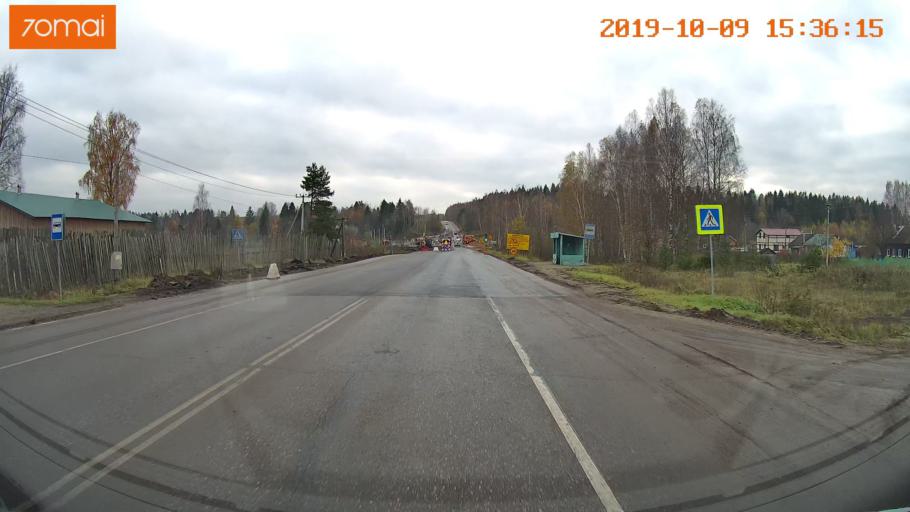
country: RU
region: Kostroma
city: Oktyabr'skiy
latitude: 57.9248
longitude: 41.2125
